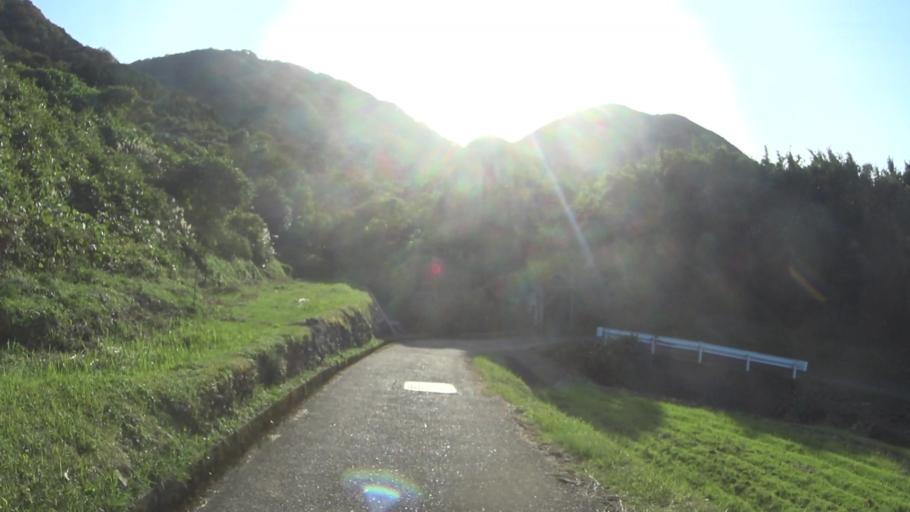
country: JP
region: Kyoto
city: Miyazu
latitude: 35.7621
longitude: 135.2068
